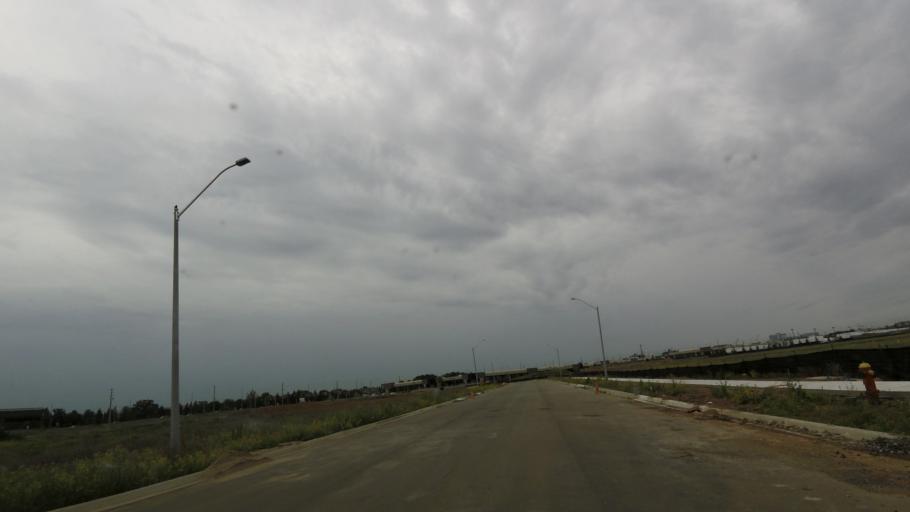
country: CA
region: Ontario
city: Oakville
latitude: 43.3878
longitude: -79.7385
